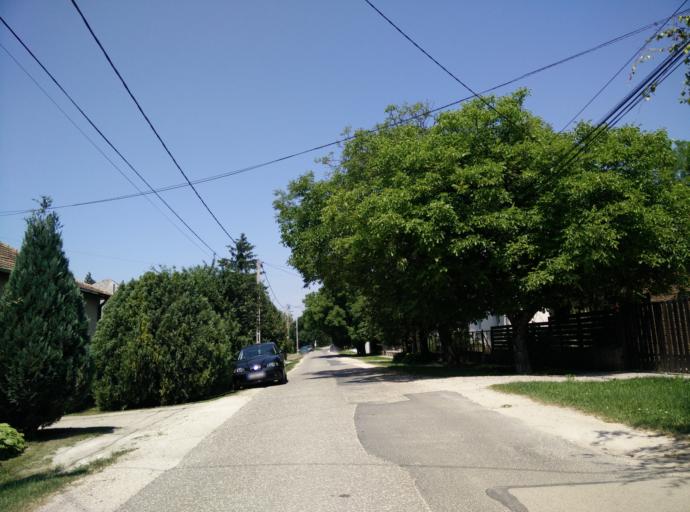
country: HU
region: Pest
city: Biatorbagy
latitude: 47.4640
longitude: 18.8194
